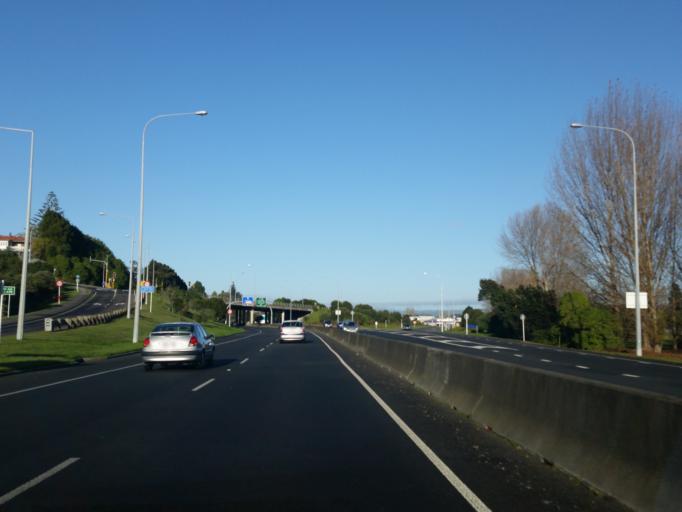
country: NZ
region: Bay of Plenty
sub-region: Tauranga City
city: Tauranga
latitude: -37.6953
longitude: 176.1554
